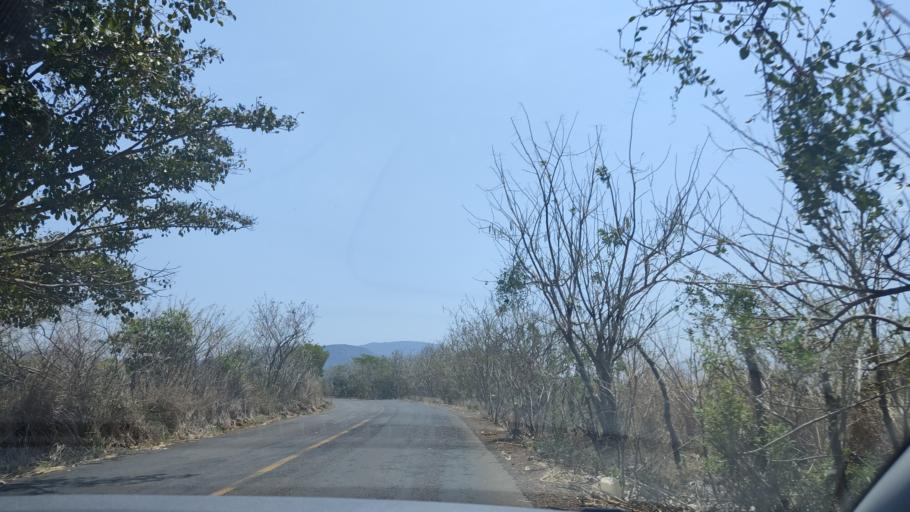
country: MX
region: Nayarit
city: Puga
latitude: 21.5807
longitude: -104.7746
